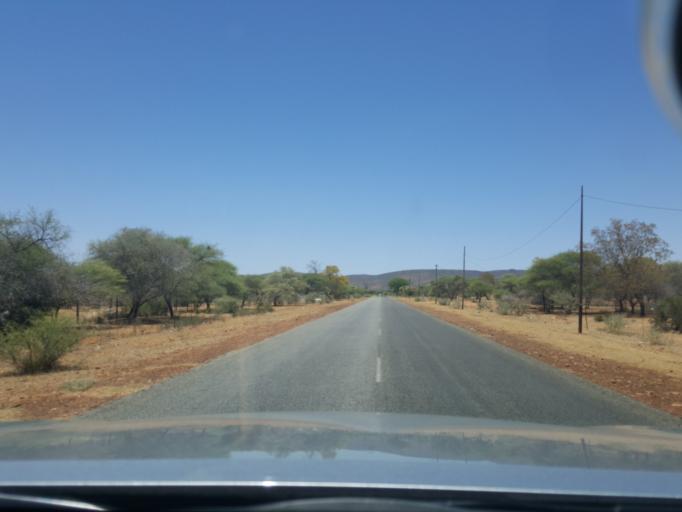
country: BW
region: South East
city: Lobatse
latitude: -25.2638
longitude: 25.9262
